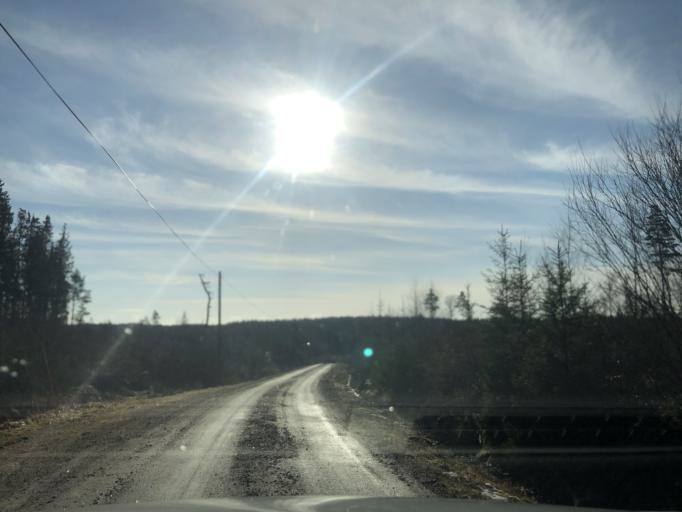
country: SE
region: Vaestra Goetaland
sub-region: Ulricehamns Kommun
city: Ulricehamn
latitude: 57.7935
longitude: 13.4666
